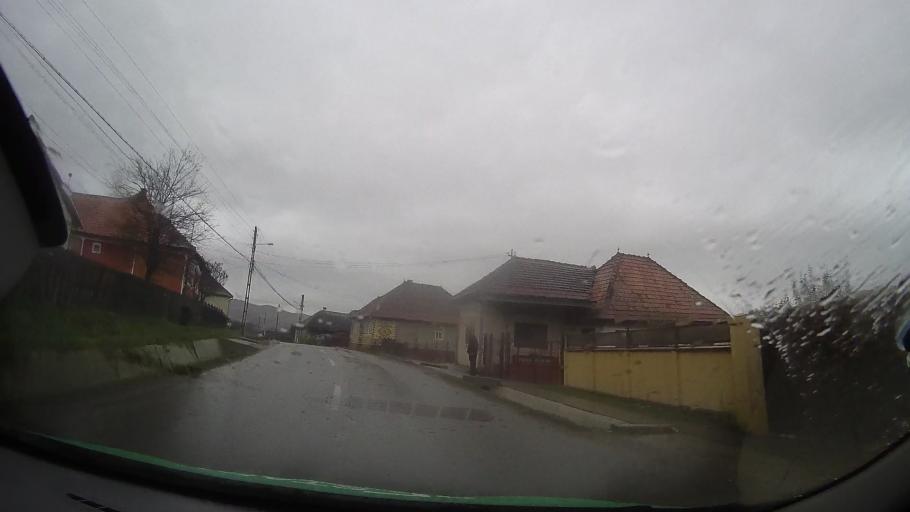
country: RO
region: Bistrita-Nasaud
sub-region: Comuna Monor
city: Monor
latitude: 46.9503
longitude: 24.7001
